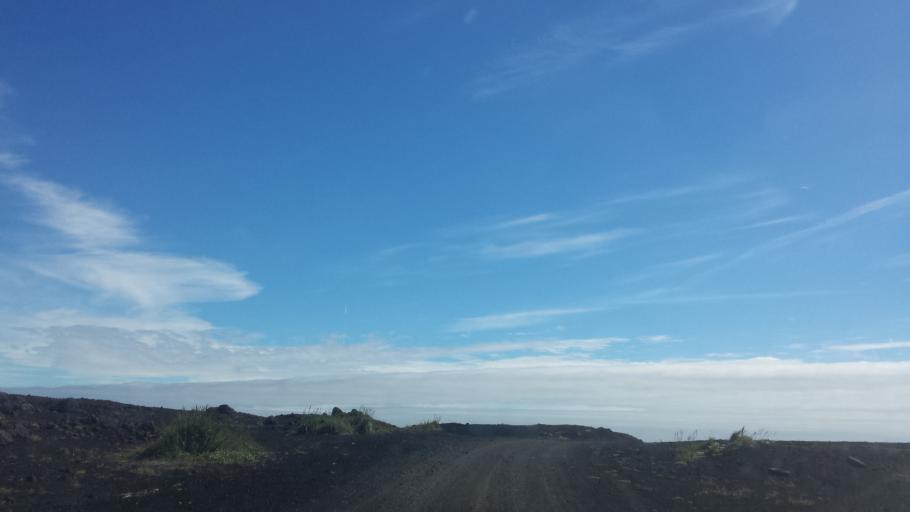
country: IS
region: South
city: Vestmannaeyjar
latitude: 63.4372
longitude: -20.2391
